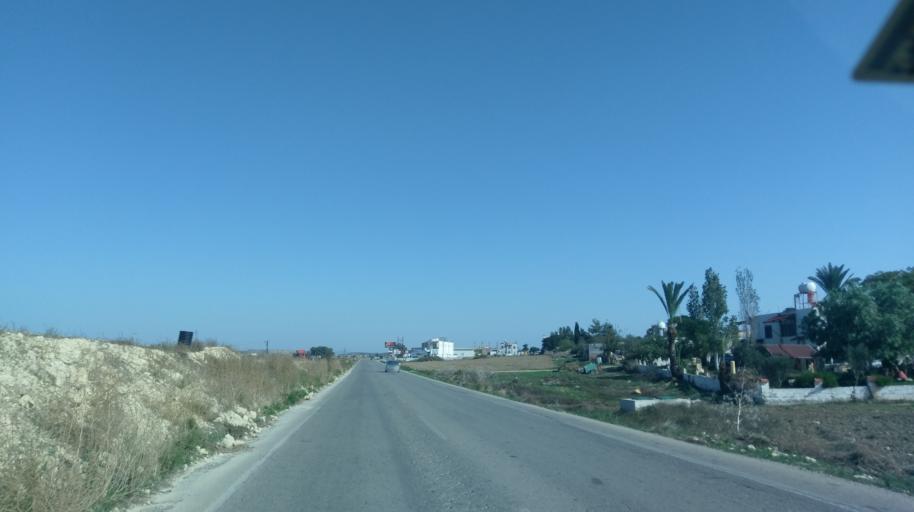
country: CY
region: Ammochostos
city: Trikomo
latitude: 35.3657
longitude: 34.0214
